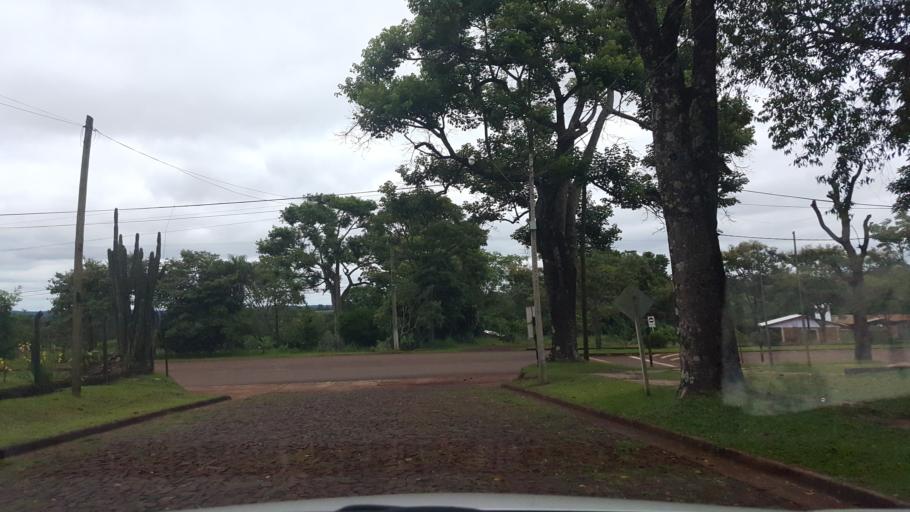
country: AR
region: Misiones
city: Ruiz de Montoya
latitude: -26.9860
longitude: -55.0485
